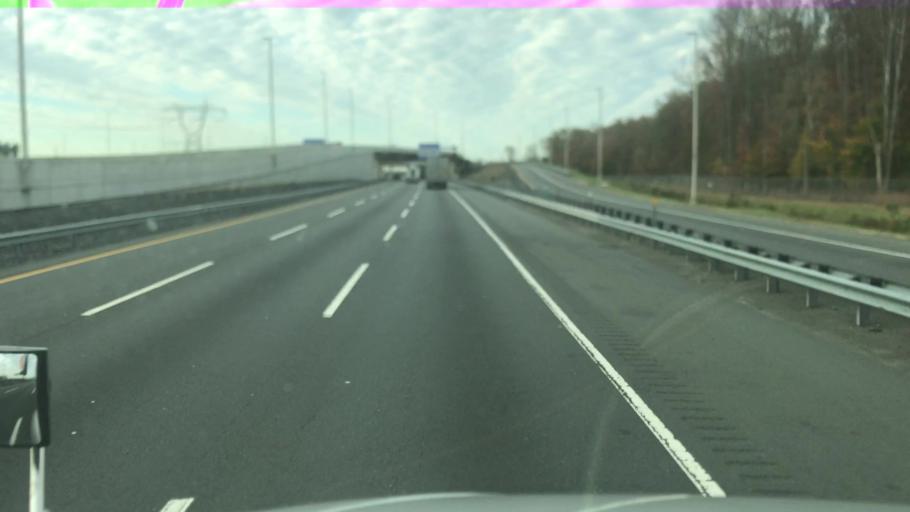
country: US
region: New Jersey
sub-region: Monmouth County
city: Allentown
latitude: 40.1997
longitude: -74.5928
